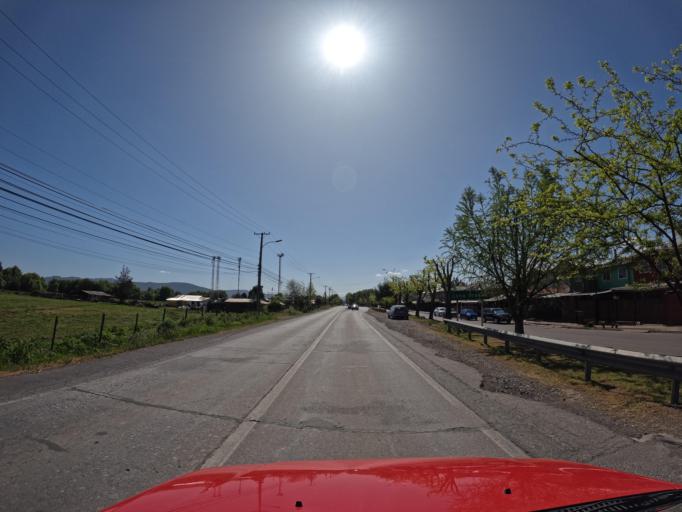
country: CL
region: Maule
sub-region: Provincia de Curico
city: Molina
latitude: -35.0616
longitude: -71.2616
